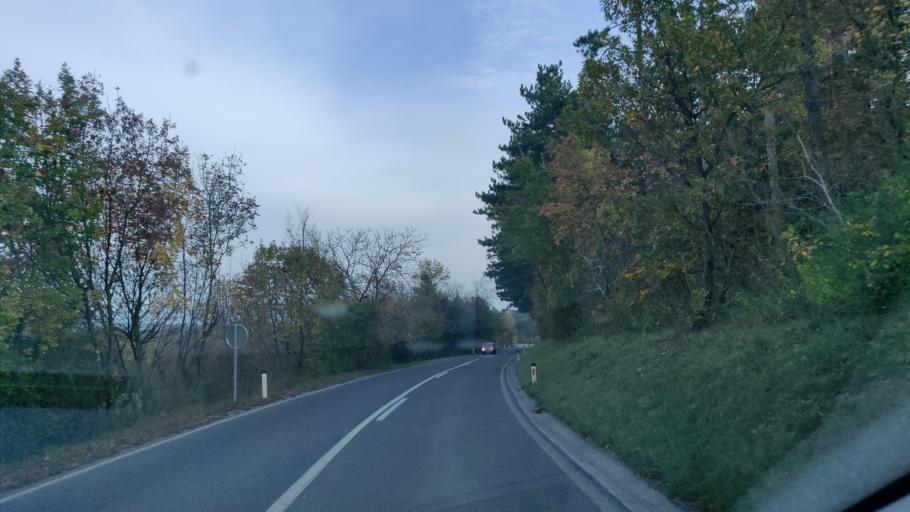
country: SI
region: Komen
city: Komen
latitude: 45.8210
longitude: 13.7533
